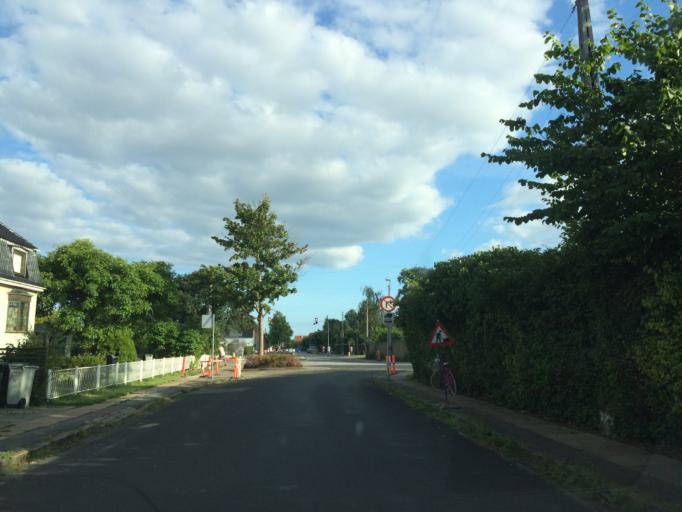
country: DK
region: Capital Region
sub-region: Kobenhavn
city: Christianshavn
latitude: 55.6571
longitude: 12.6291
